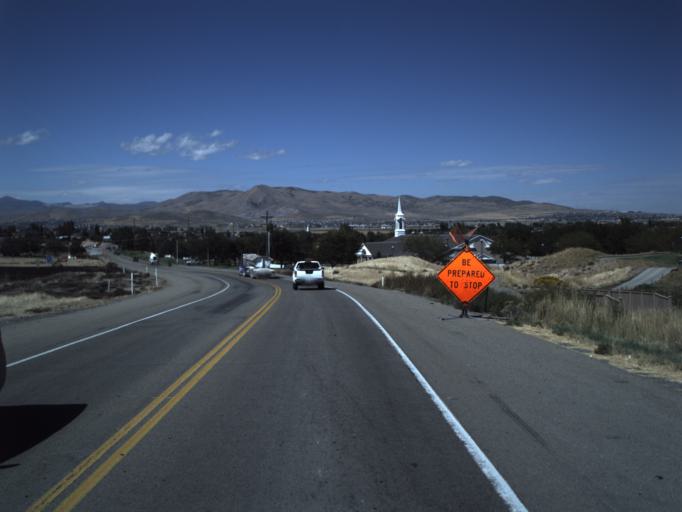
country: US
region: Utah
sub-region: Utah County
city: Saratoga Springs
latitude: 40.3299
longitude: -111.9085
